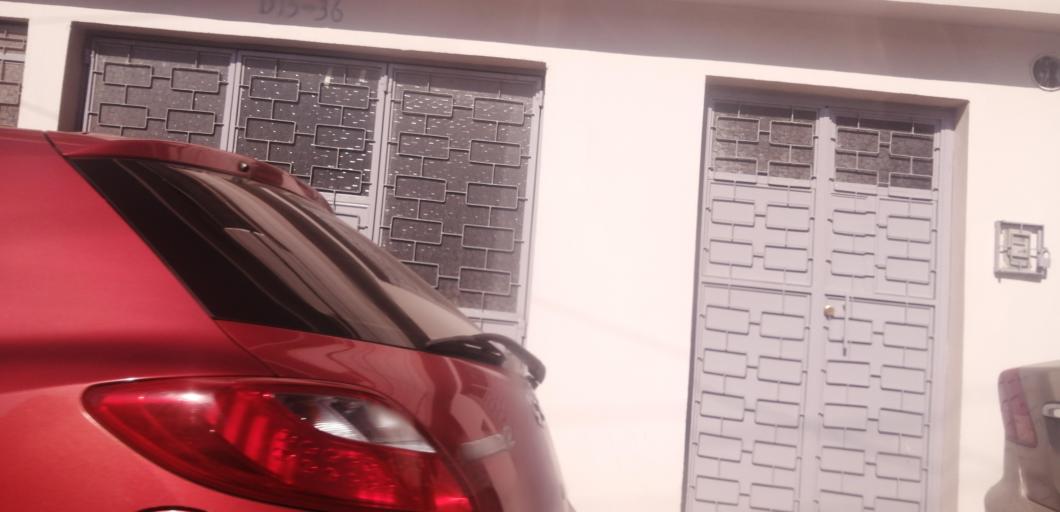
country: GT
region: Quetzaltenango
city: Quetzaltenango
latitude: 14.8427
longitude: -91.5337
